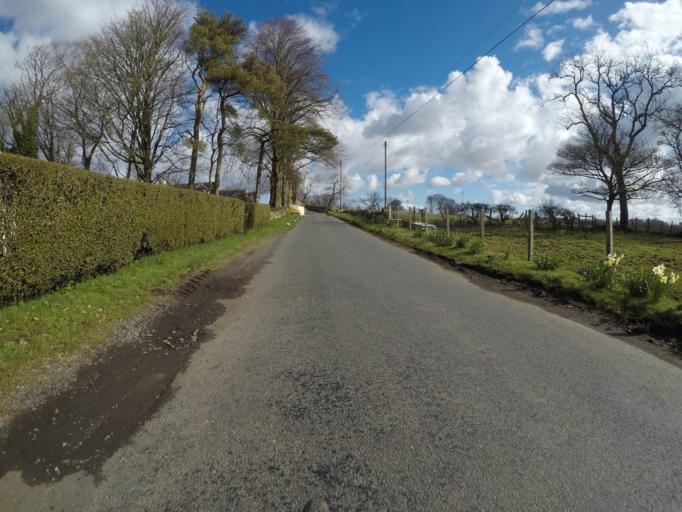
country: GB
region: Scotland
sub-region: North Ayrshire
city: Beith
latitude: 55.7196
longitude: -4.6189
